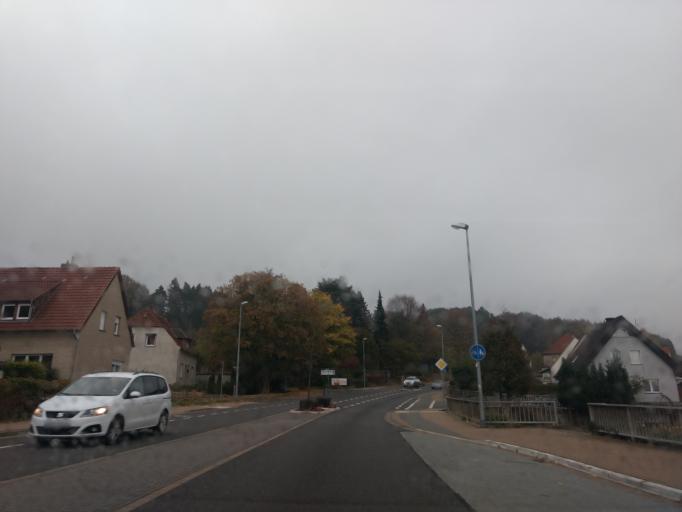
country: DE
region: Lower Saxony
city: Bad Iburg
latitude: 52.1639
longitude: 8.0512
